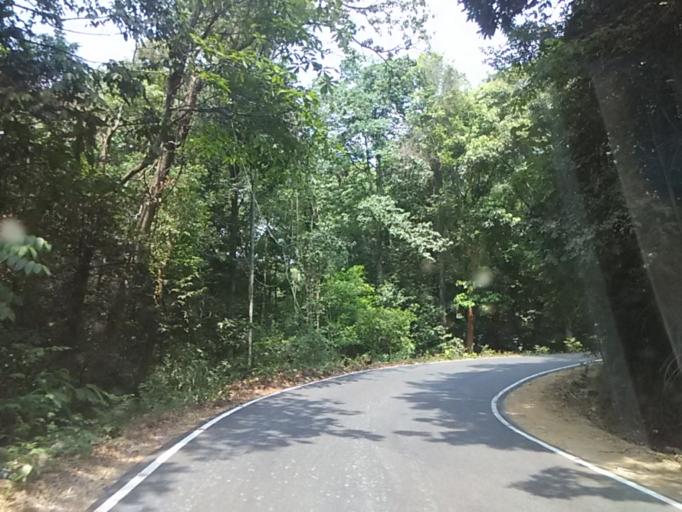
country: IN
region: Karnataka
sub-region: Kodagu
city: Virarajendrapet
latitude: 12.1112
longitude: 75.7837
